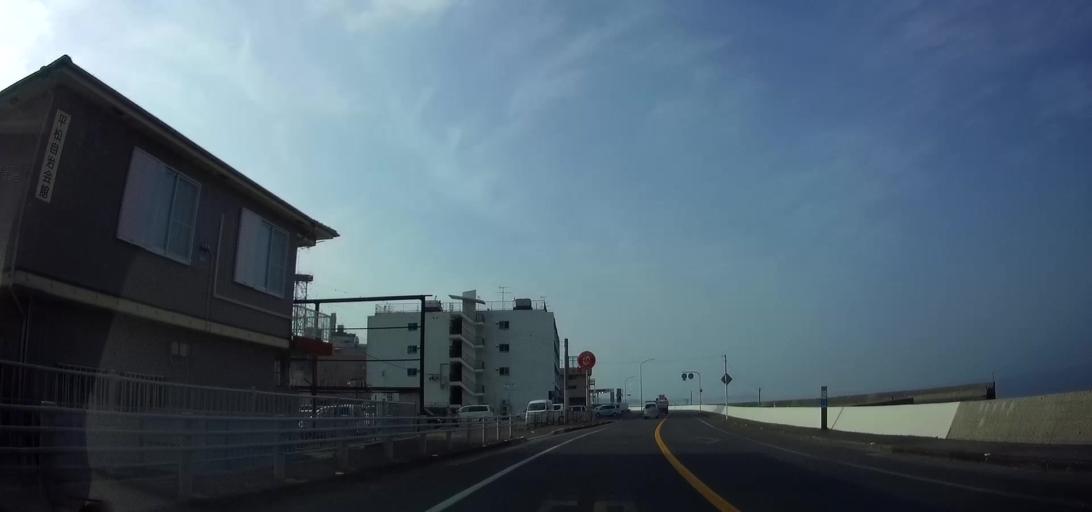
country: JP
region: Nagasaki
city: Shimabara
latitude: 32.7333
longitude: 130.2082
